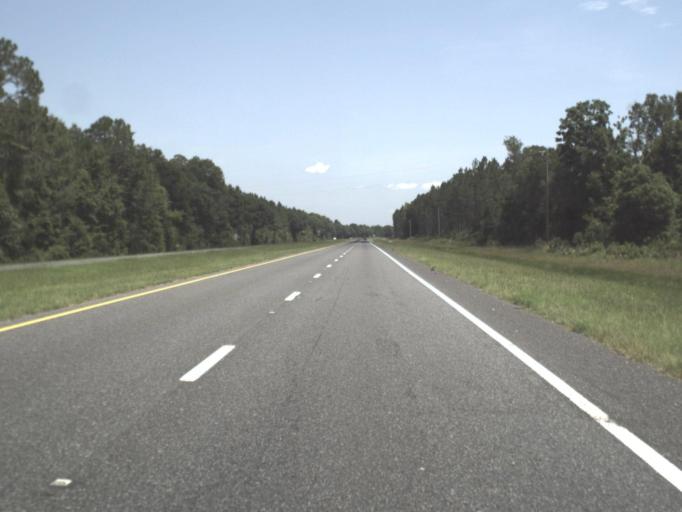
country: US
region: Florida
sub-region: Taylor County
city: Steinhatchee
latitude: 29.7401
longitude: -83.3179
